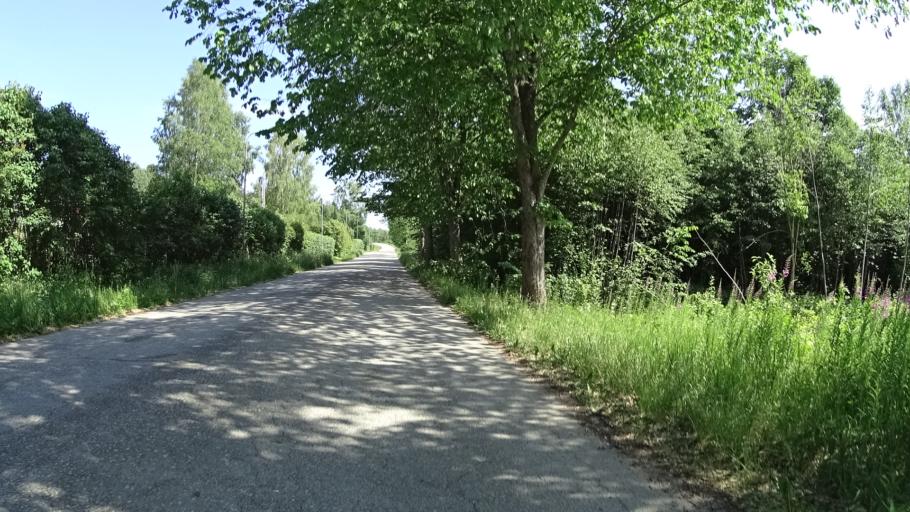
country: FI
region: Uusimaa
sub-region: Raaseporin
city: Karis
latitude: 60.0856
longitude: 23.6464
